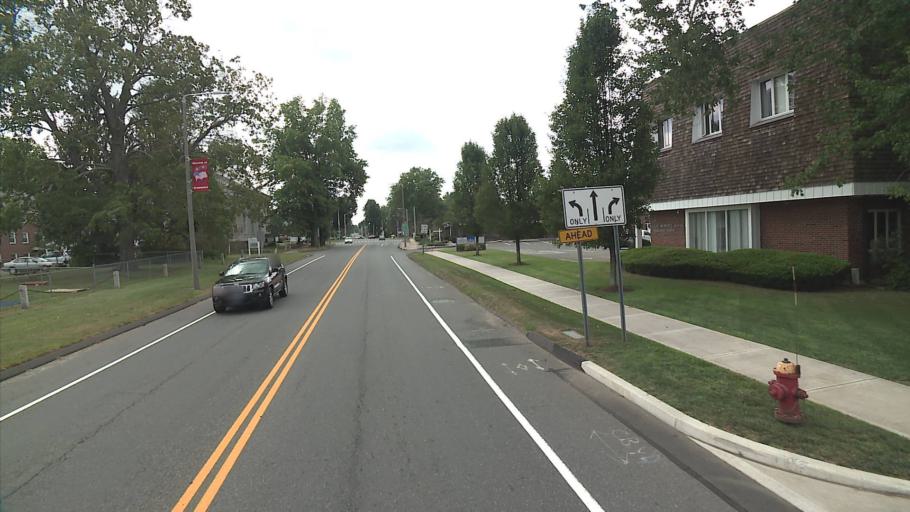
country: US
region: Connecticut
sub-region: Hartford County
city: Blue Hills
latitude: 41.8328
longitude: -72.7374
